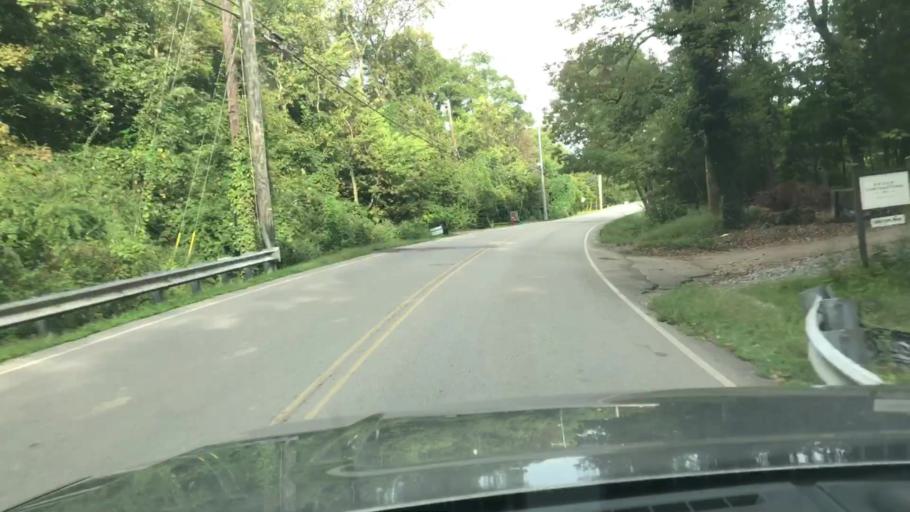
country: US
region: Tennessee
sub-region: Davidson County
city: Forest Hills
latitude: 36.0709
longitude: -86.8299
